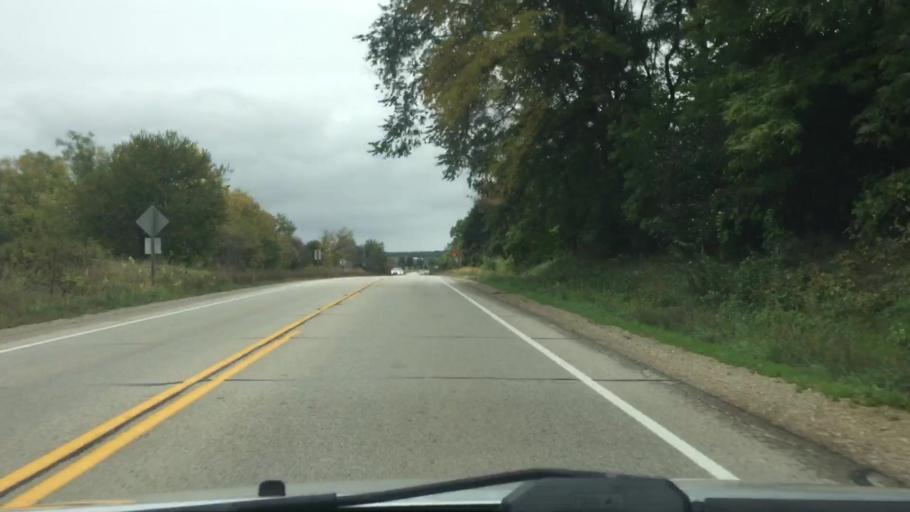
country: US
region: Wisconsin
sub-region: Walworth County
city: Elkhorn
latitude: 42.7392
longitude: -88.5506
